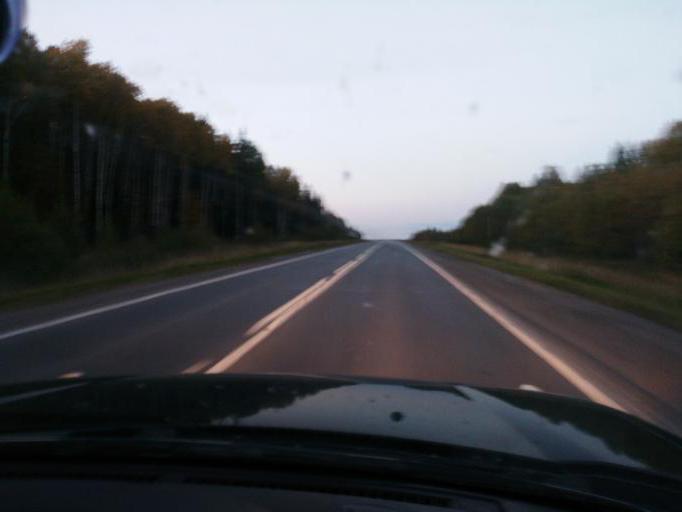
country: RU
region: Perm
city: Verkhnechusovskiye Gorodki
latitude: 58.2291
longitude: 57.2072
